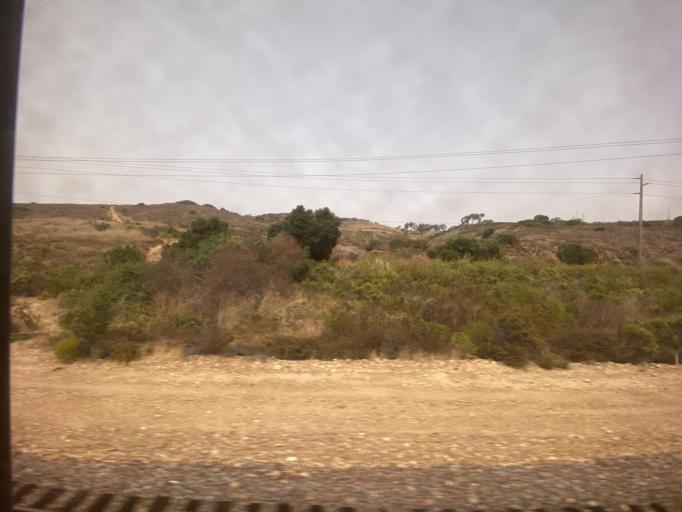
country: US
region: California
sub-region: San Diego County
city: La Jolla
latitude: 32.8633
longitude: -117.1928
